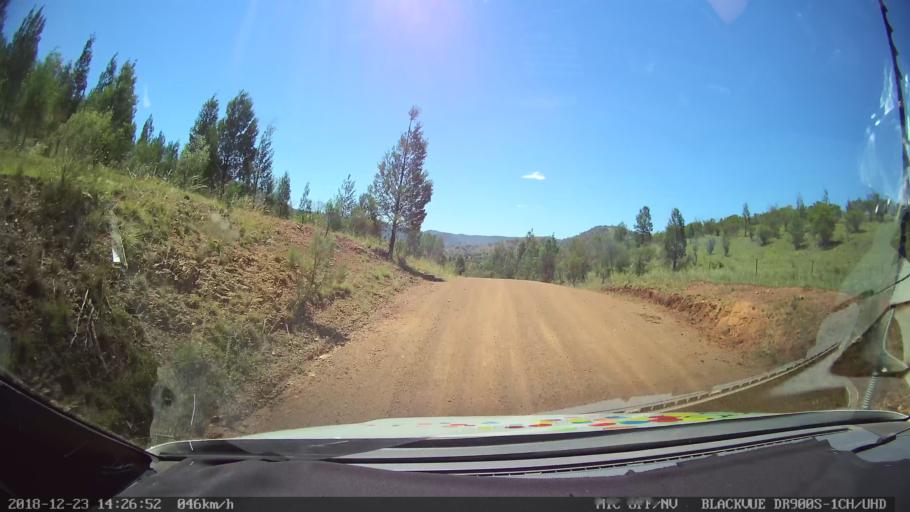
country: AU
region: New South Wales
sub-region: Tamworth Municipality
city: Manilla
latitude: -30.6209
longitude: 150.9505
